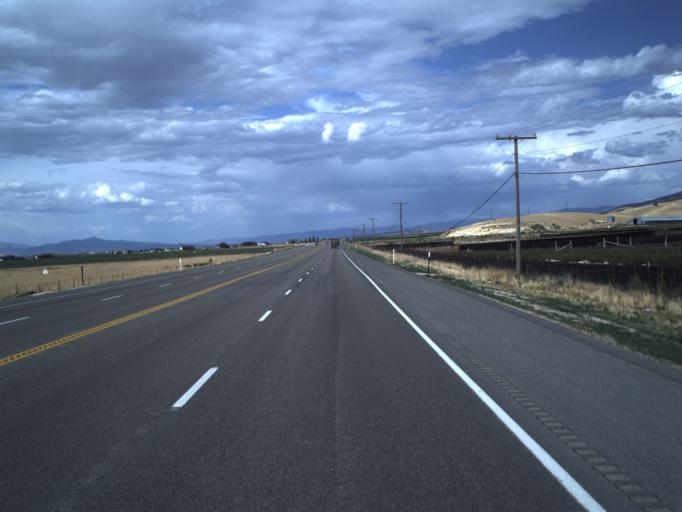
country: US
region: Utah
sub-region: Sanpete County
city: Manti
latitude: 39.2935
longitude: -111.6225
